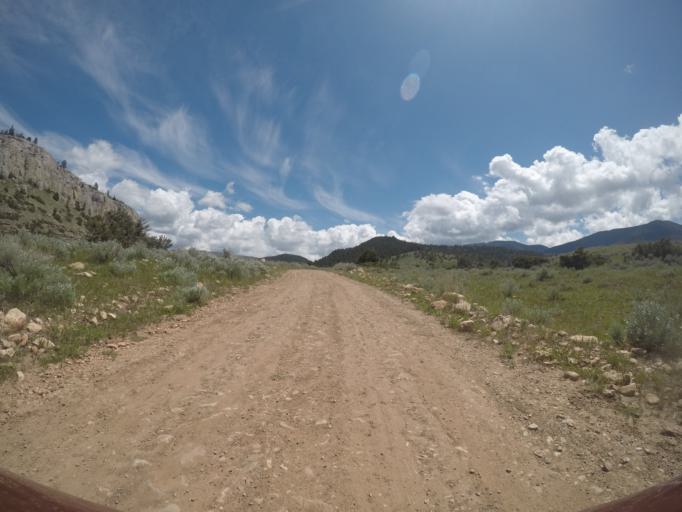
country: US
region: Wyoming
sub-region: Big Horn County
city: Lovell
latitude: 45.2231
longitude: -108.5932
